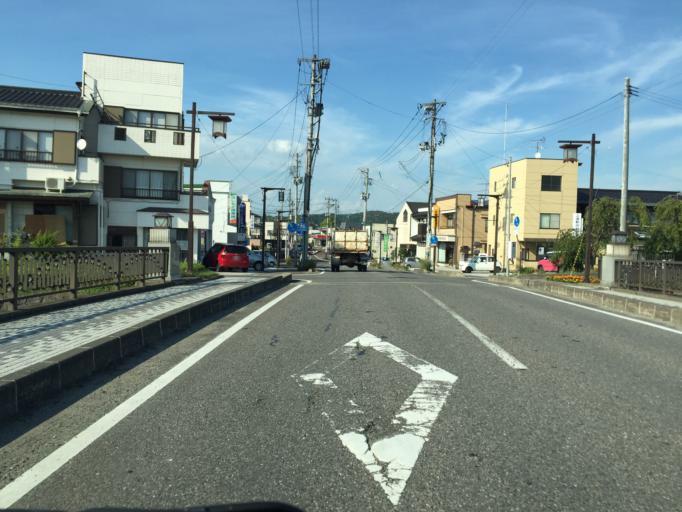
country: JP
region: Fukushima
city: Motomiya
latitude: 37.5167
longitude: 140.4039
